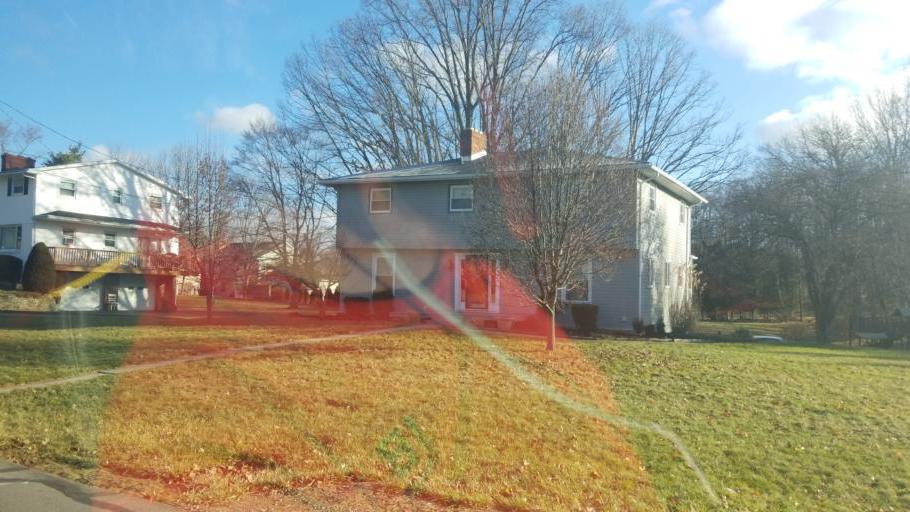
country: US
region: Ohio
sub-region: Richland County
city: Ontario
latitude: 40.7553
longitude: -82.5978
